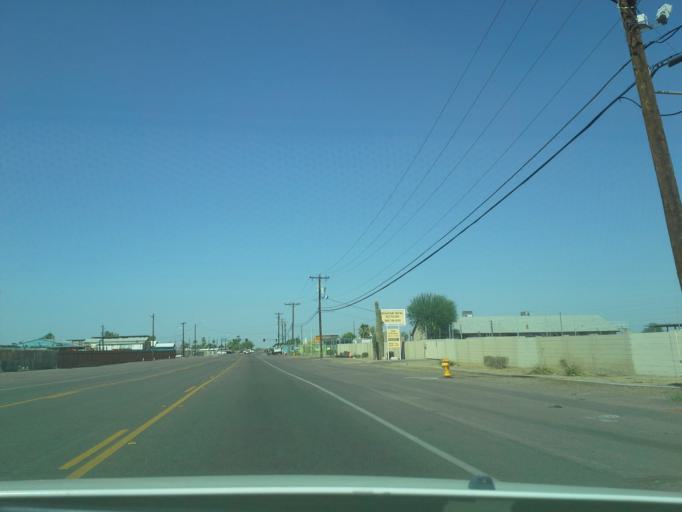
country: US
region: Arizona
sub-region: Maricopa County
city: Laveen
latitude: 33.4067
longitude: -112.1302
